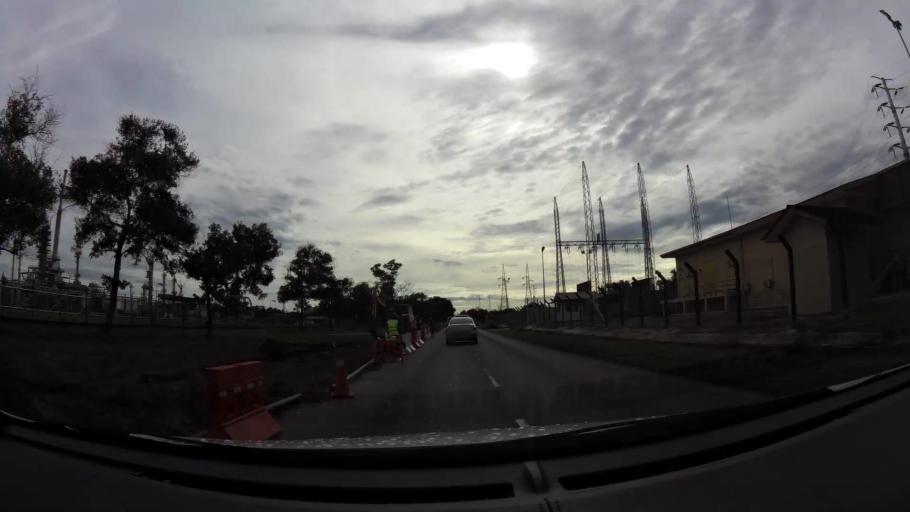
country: BN
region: Belait
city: Seria
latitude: 4.6162
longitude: 114.3431
